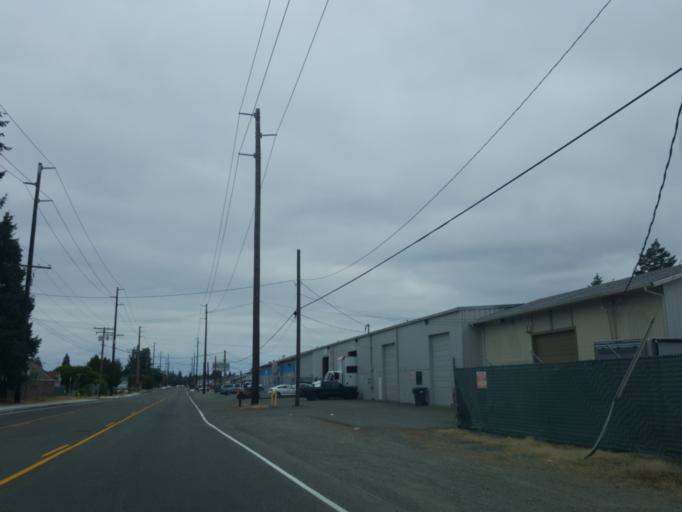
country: US
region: Washington
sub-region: Pierce County
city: Lakewood
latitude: 47.1601
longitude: -122.4950
